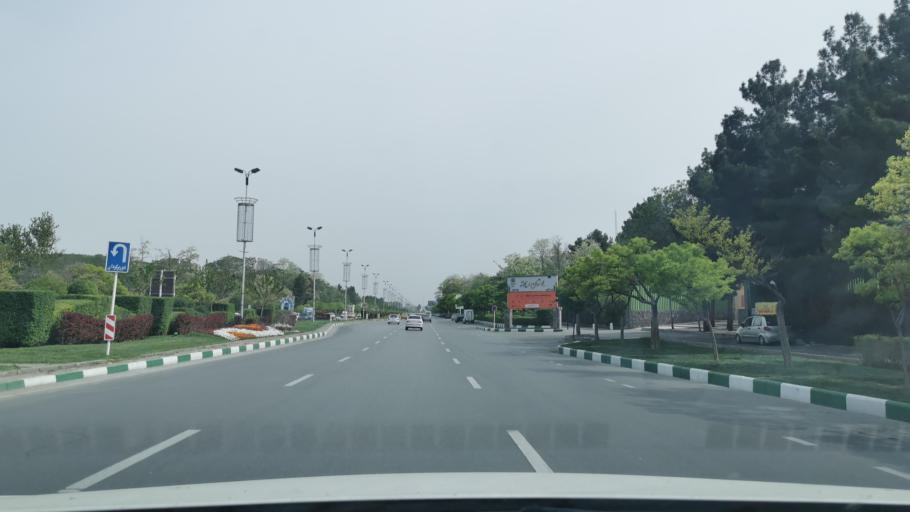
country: IR
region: Razavi Khorasan
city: Mashhad
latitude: 36.2514
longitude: 59.6151
